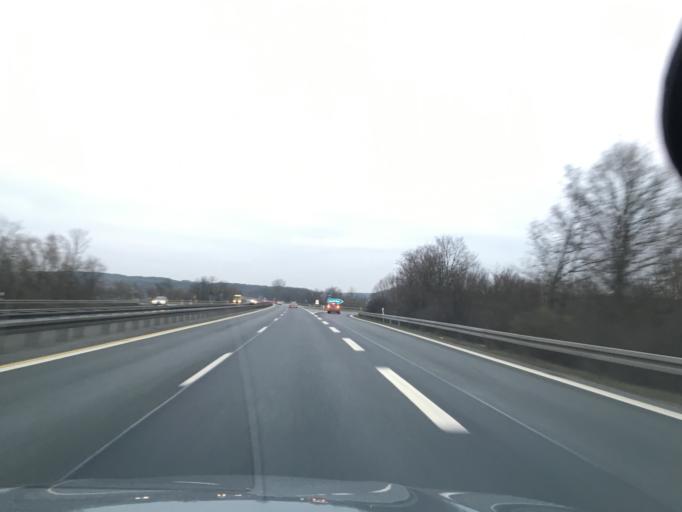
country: DE
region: Bavaria
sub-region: Regierungsbezirk Mittelfranken
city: Gremsdorf
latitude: 49.6993
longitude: 10.8556
